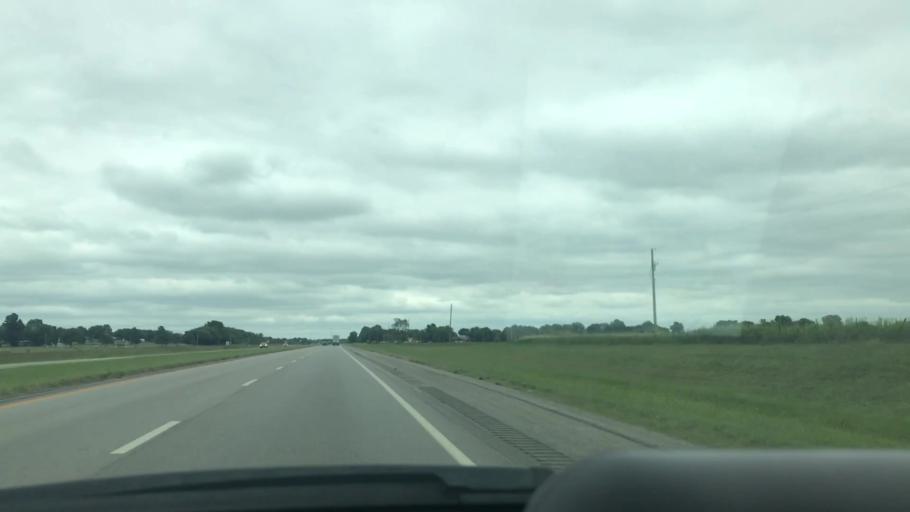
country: US
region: Oklahoma
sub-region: Mayes County
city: Pryor
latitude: 36.3308
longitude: -95.3100
